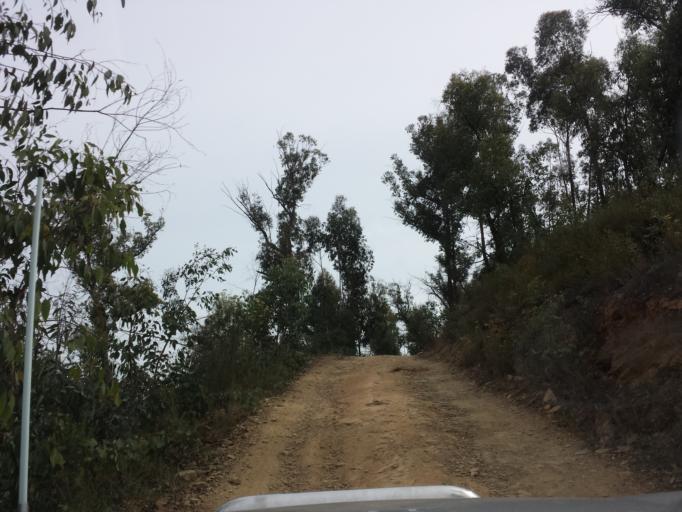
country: AU
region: Victoria
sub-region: Wellington
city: Heyfield
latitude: -37.7561
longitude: 146.4023
